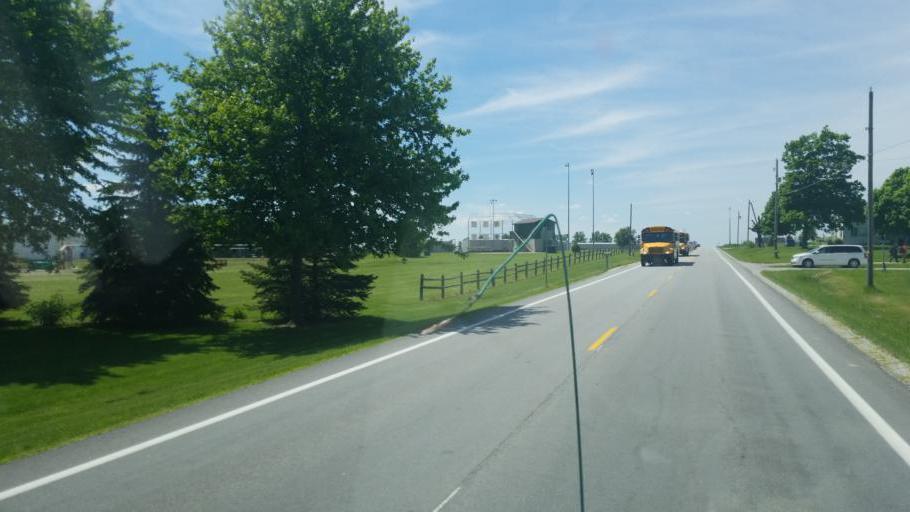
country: US
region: Ohio
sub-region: Huron County
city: Willard
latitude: 41.0672
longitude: -82.8944
